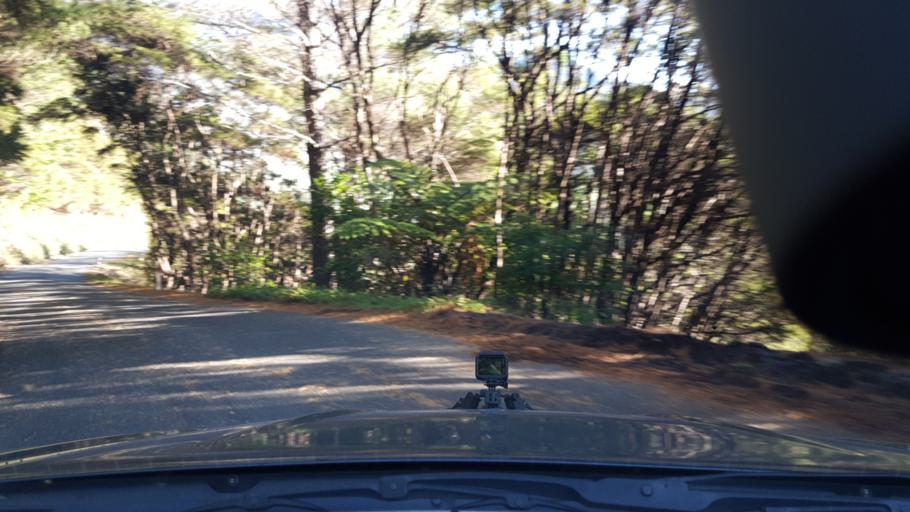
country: NZ
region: Marlborough
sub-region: Marlborough District
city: Picton
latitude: -41.1772
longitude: 173.9754
